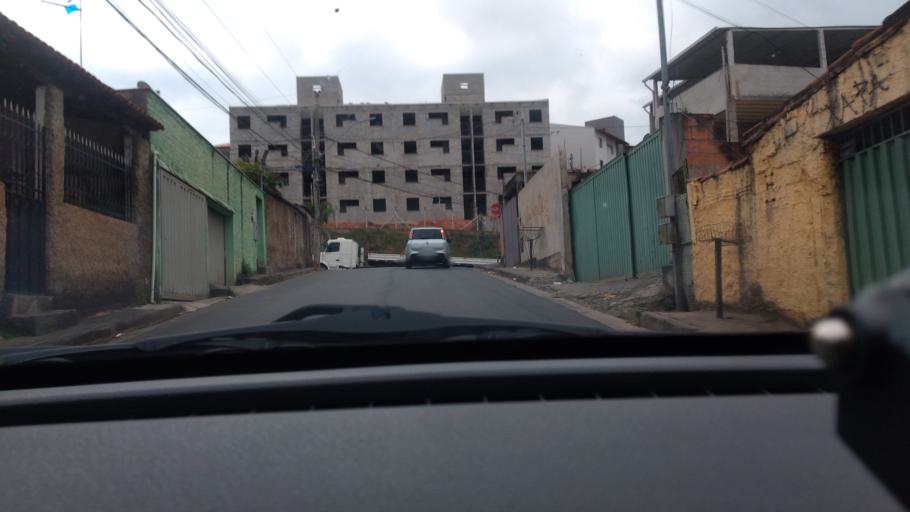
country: BR
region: Minas Gerais
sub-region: Santa Luzia
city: Santa Luzia
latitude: -19.8196
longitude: -43.9381
